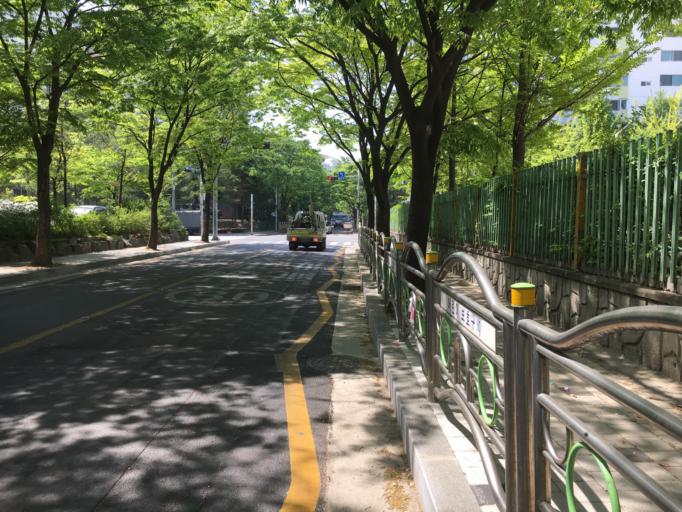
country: KR
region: Gyeonggi-do
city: Kwangmyong
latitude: 37.5610
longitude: 126.8485
